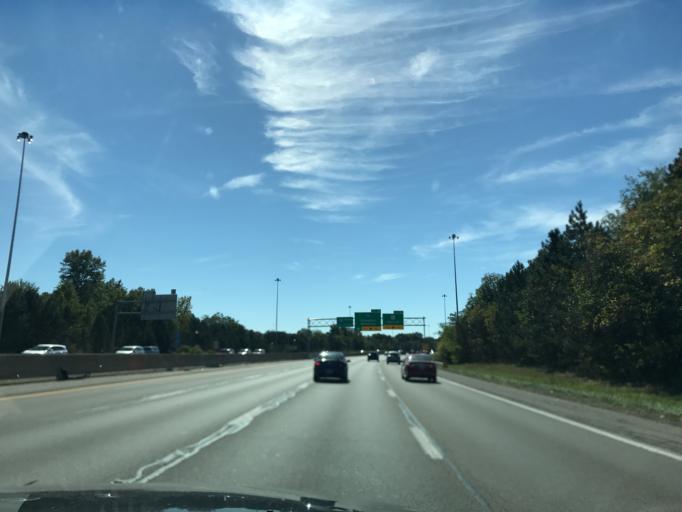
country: US
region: Ohio
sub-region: Franklin County
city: Reynoldsburg
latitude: 39.9689
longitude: -82.8446
